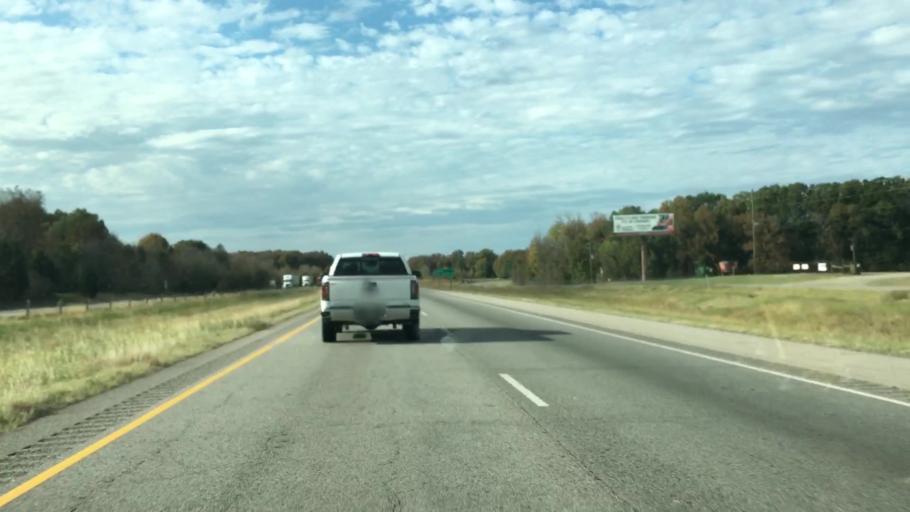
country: US
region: Arkansas
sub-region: Pope County
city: Atkins
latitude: 35.2250
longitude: -92.8374
